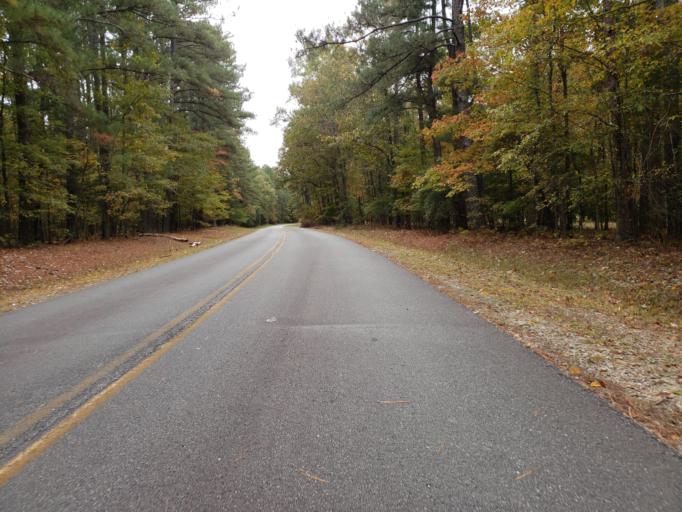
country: US
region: North Carolina
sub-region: Chatham County
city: Fearrington Village
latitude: 35.7607
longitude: -79.0446
